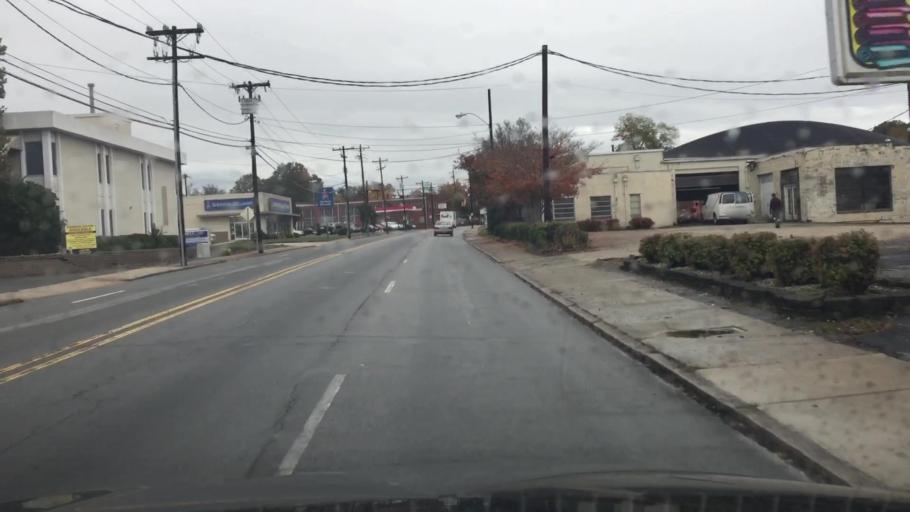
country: US
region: North Carolina
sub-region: Rowan County
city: Salisbury
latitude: 35.6740
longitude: -80.4783
